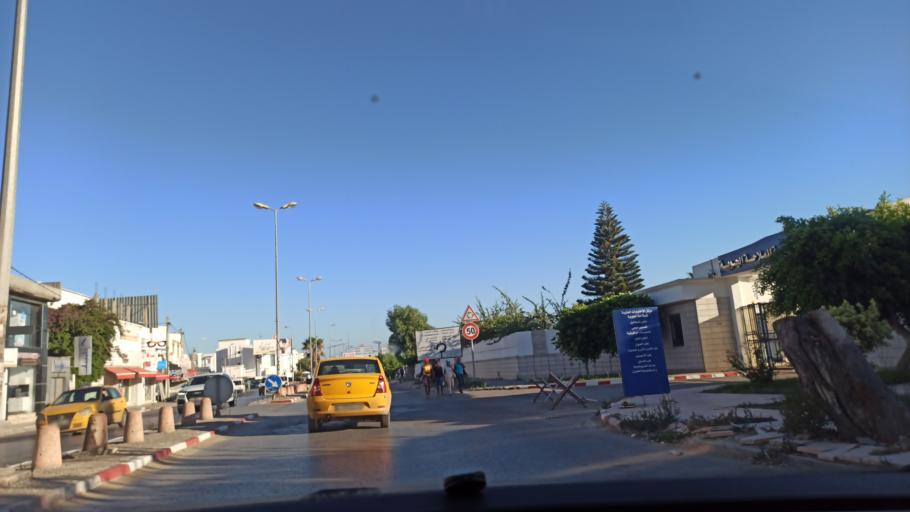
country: TN
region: Tunis
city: La Goulette
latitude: 36.8506
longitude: 10.2587
